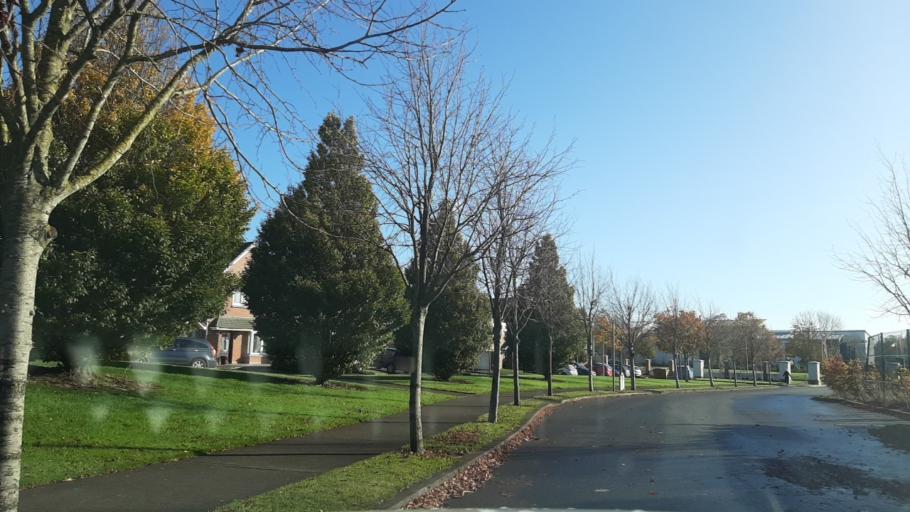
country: IE
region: Leinster
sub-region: Kildare
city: Rathangan
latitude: 53.2229
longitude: -7.0065
